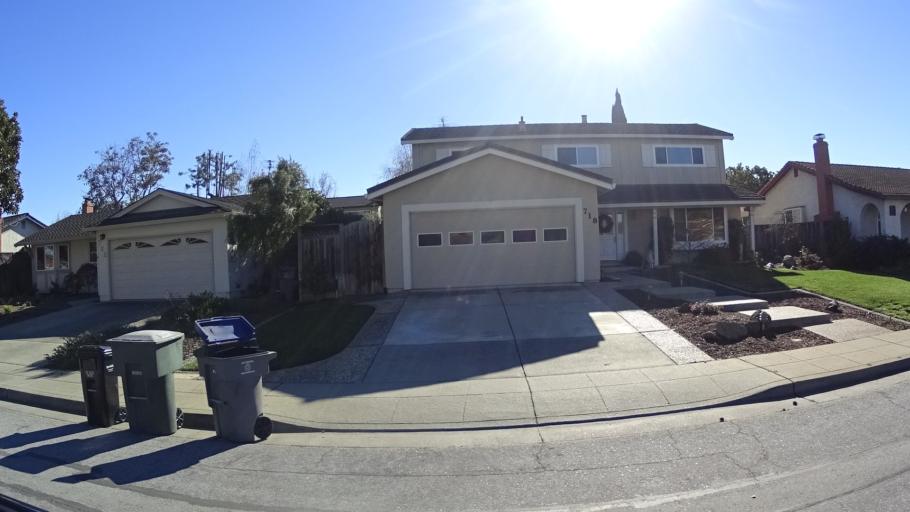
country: US
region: California
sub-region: Santa Clara County
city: Cupertino
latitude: 37.3399
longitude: -122.0220
